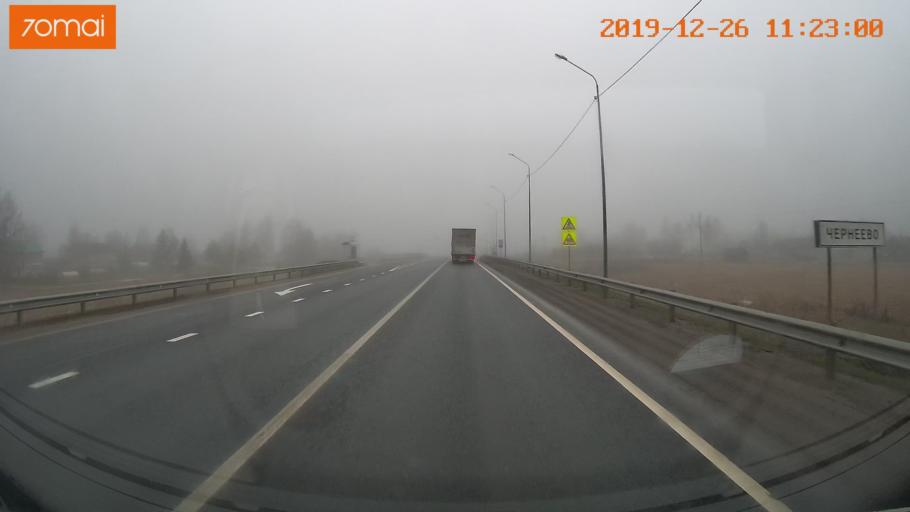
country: RU
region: Vologda
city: Chebsara
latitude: 59.1308
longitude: 38.9311
